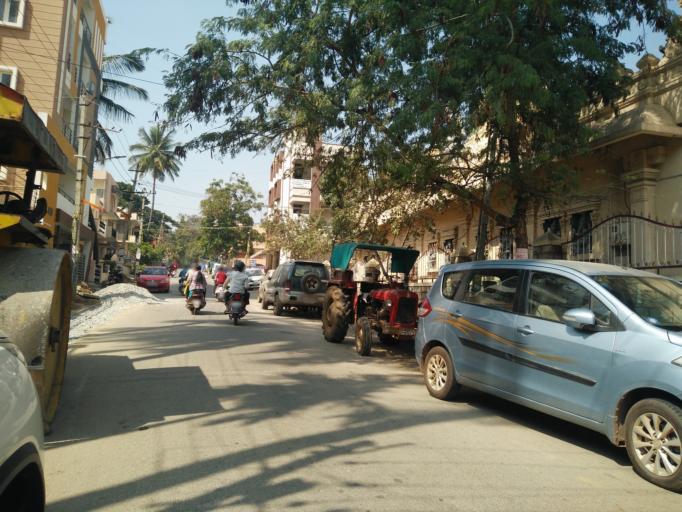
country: IN
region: Karnataka
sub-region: Bangalore Urban
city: Bangalore
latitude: 12.9724
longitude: 77.5465
